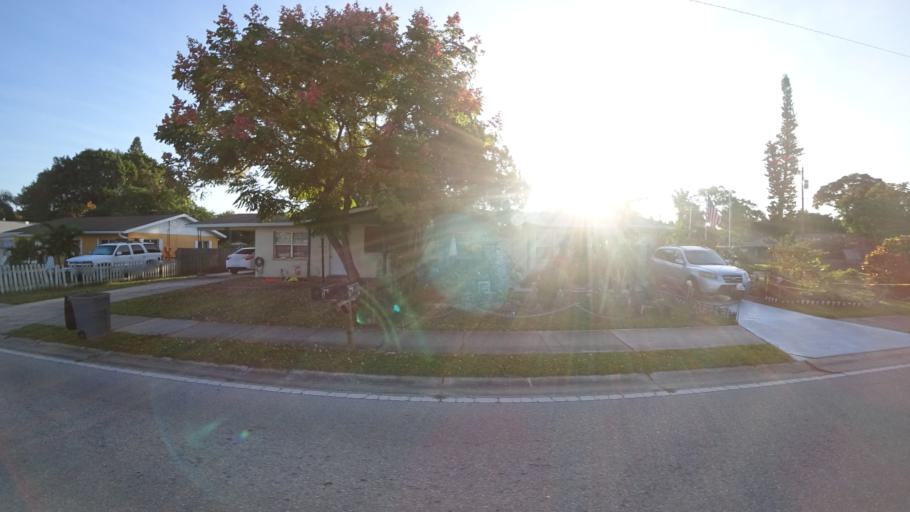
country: US
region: Florida
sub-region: Manatee County
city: South Bradenton
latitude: 27.4572
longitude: -82.5820
